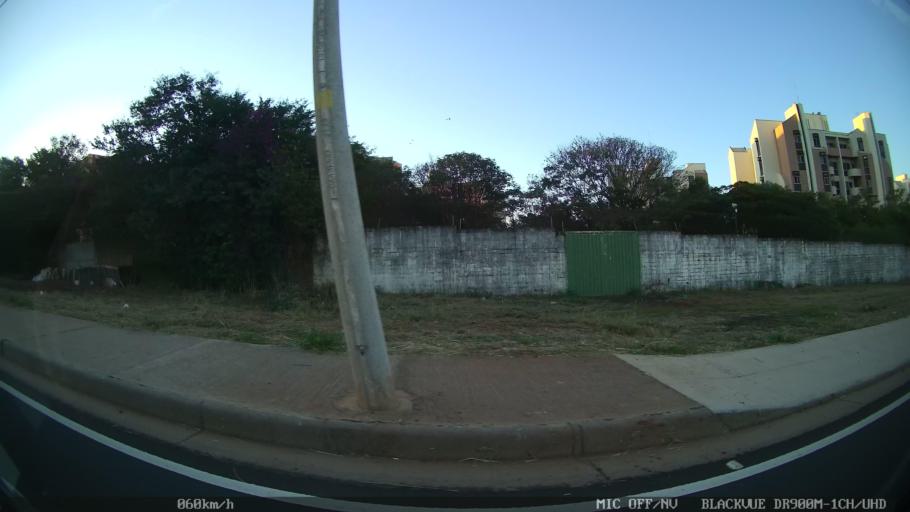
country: BR
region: Sao Paulo
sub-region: Sao Jose Do Rio Preto
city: Sao Jose do Rio Preto
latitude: -20.8487
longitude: -49.3961
